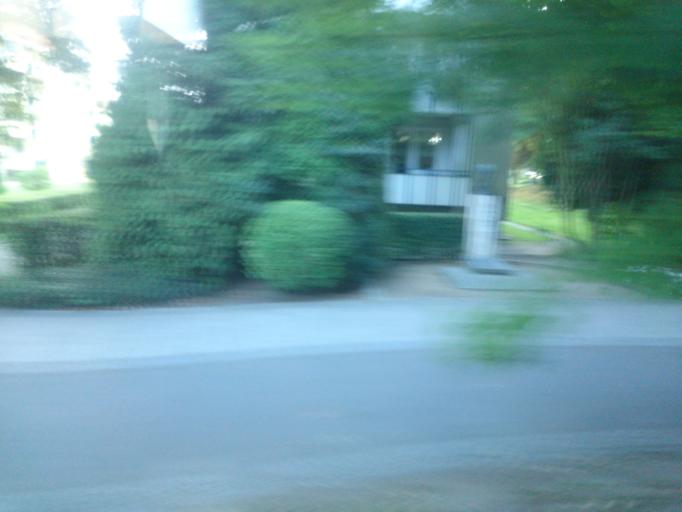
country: DE
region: Mecklenburg-Vorpommern
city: Anklam
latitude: 53.8568
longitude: 13.6889
